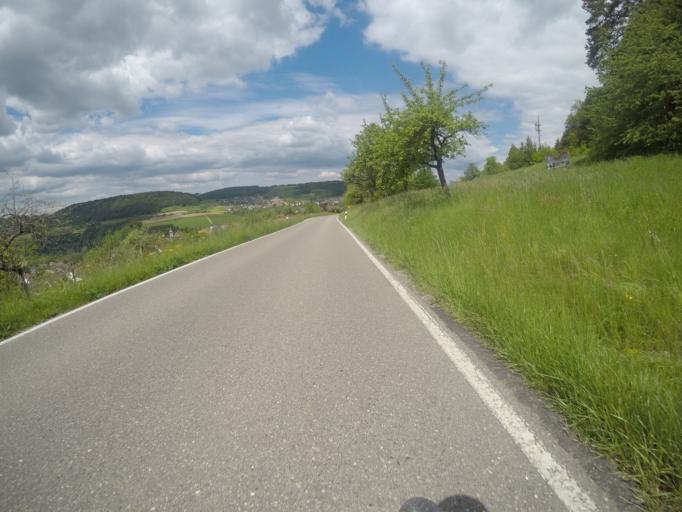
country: DE
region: Baden-Wuerttemberg
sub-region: Karlsruhe Region
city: Nagold
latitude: 48.5827
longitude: 8.7394
